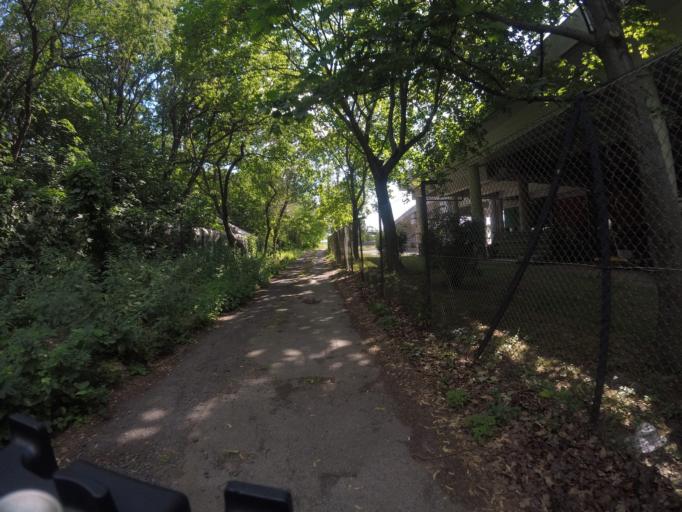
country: DE
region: Berlin
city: Haselhorst
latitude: 52.5296
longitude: 13.2408
